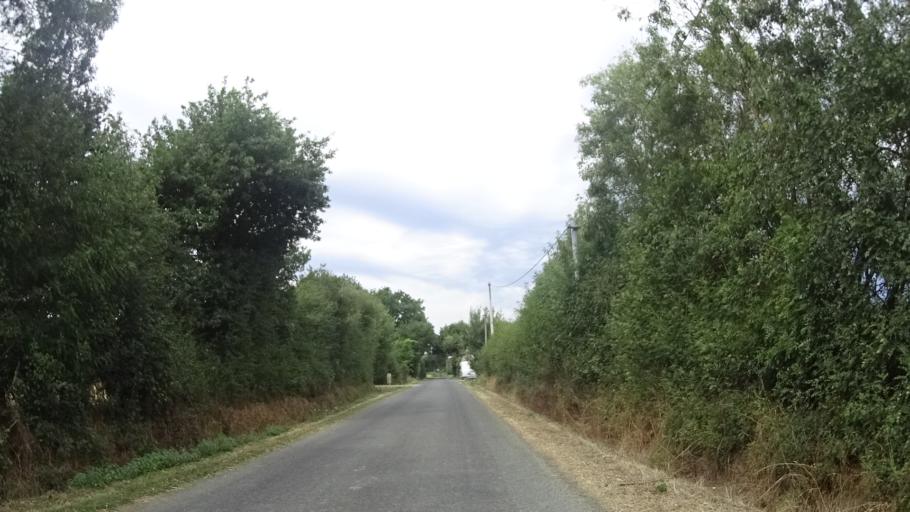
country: FR
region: Pays de la Loire
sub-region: Departement de la Loire-Atlantique
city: Blain
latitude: 47.4311
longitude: -1.7443
